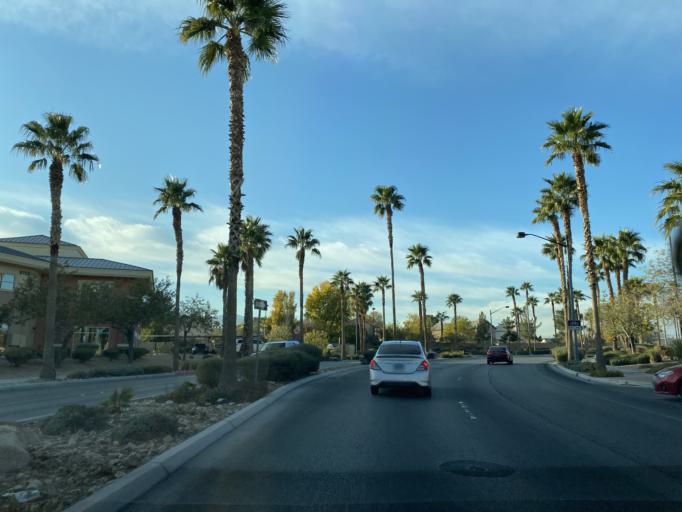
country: US
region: Nevada
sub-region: Clark County
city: Las Vegas
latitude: 36.2655
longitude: -115.2597
